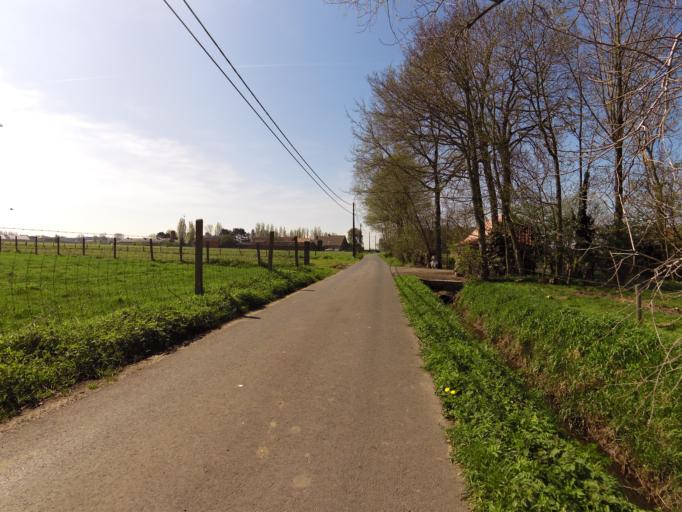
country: BE
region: Flanders
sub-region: Provincie West-Vlaanderen
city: Ichtegem
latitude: 51.1284
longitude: 3.0001
